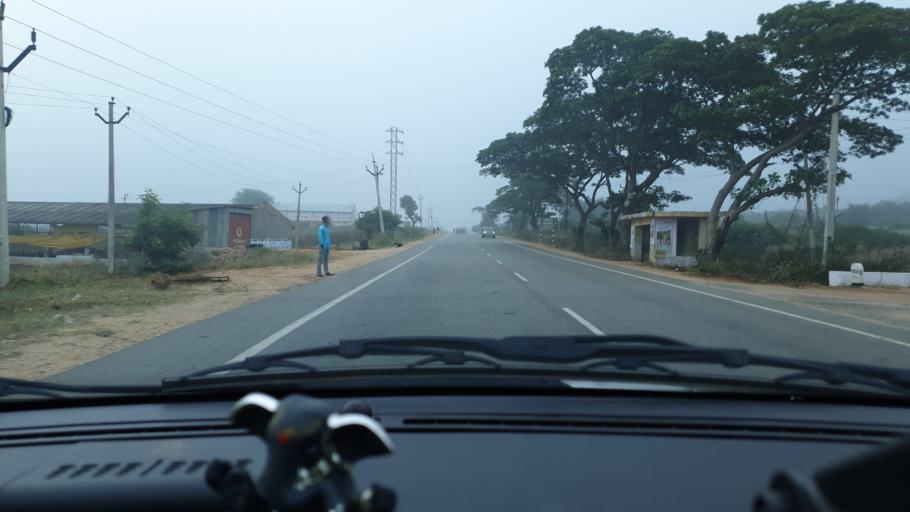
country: IN
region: Telangana
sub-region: Mahbubnagar
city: Farrukhnagar
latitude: 16.9224
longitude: 78.5272
